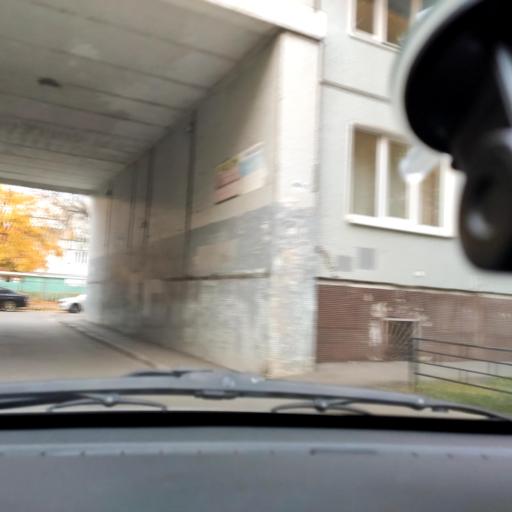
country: RU
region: Samara
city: Tol'yatti
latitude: 53.5303
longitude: 49.3317
